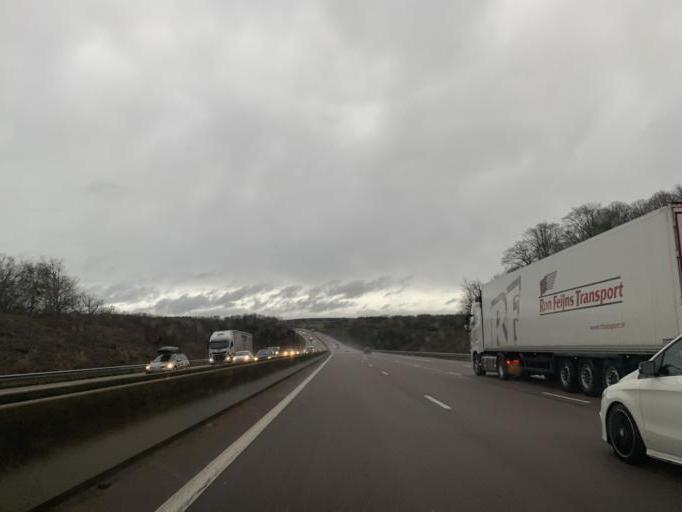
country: FR
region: Bourgogne
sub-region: Departement de la Cote-d'Or
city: Selongey
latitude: 47.7393
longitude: 5.1948
